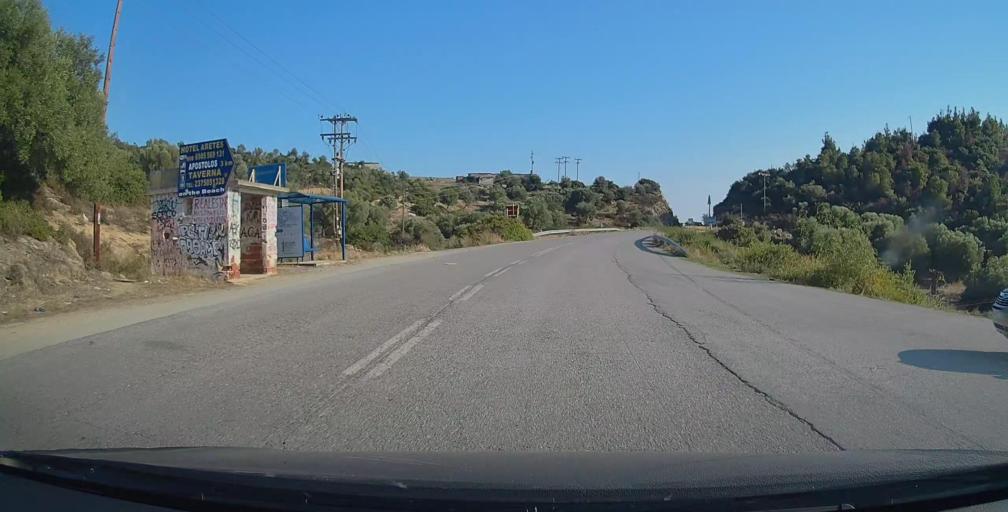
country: GR
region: Central Macedonia
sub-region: Nomos Chalkidikis
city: Sykia
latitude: 40.0015
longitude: 23.8880
